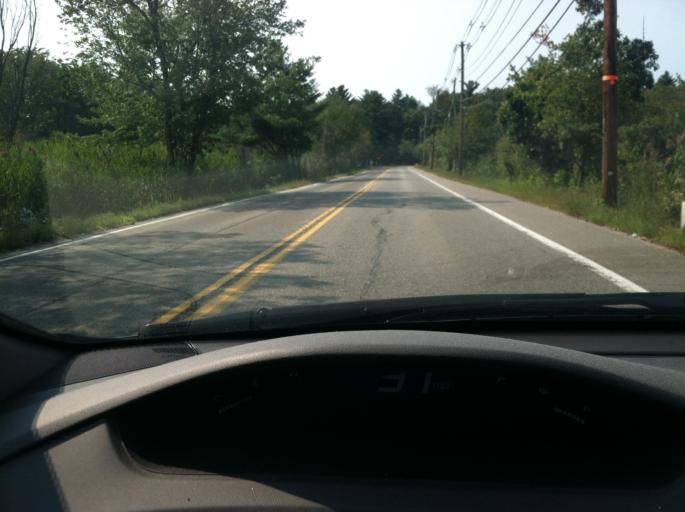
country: US
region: Massachusetts
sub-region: Middlesex County
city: Bedford
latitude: 42.4979
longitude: -71.2877
